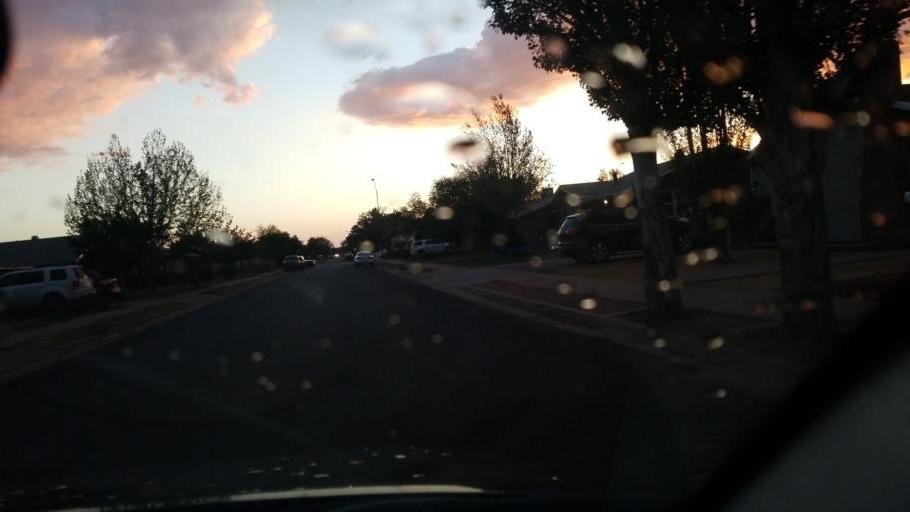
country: US
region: Arizona
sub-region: Navajo County
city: Winslow
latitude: 35.0326
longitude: -110.6966
